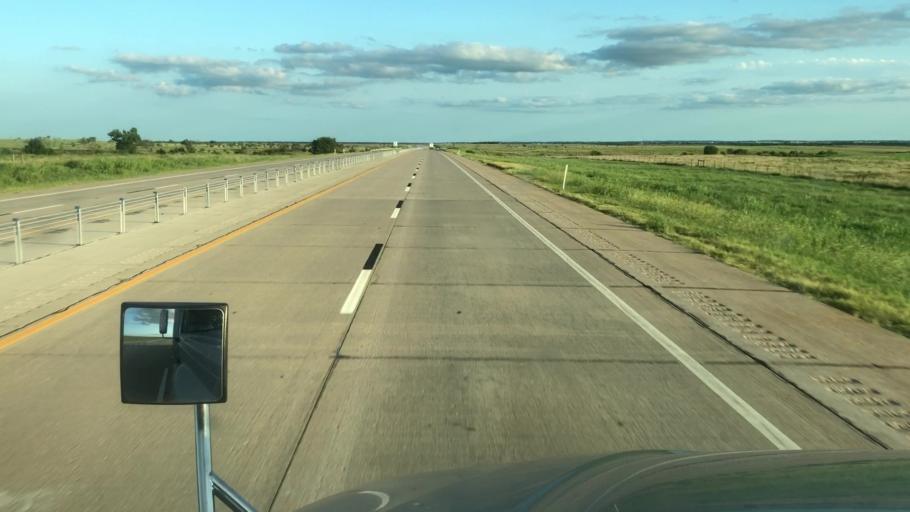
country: US
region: Oklahoma
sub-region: Pawnee County
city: Pawnee
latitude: 36.3624
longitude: -97.0337
